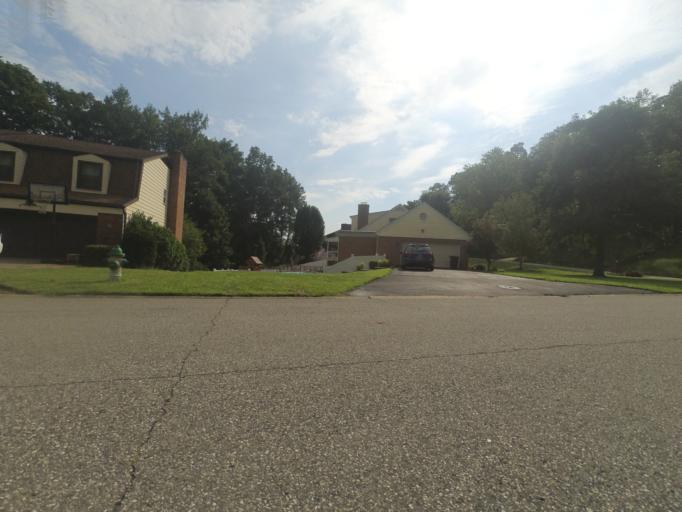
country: US
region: West Virginia
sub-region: Cabell County
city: Huntington
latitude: 38.4012
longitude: -82.4196
